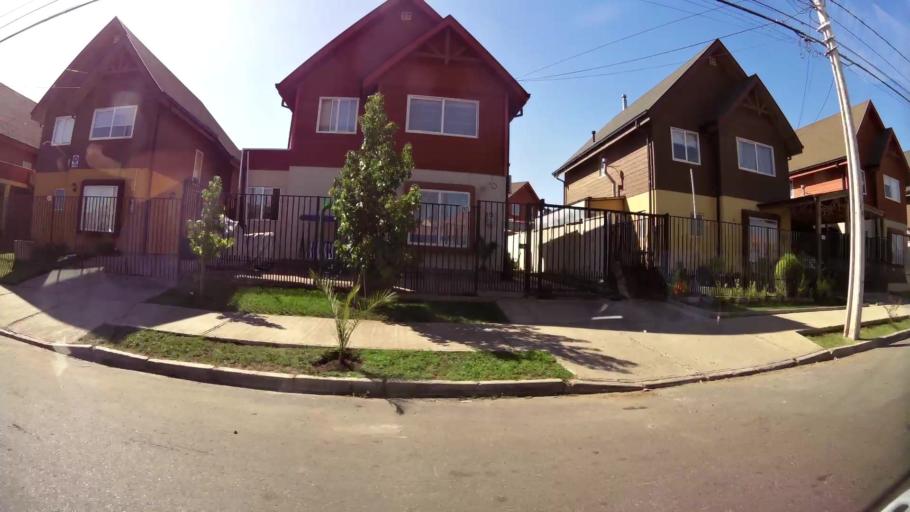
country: CL
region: Maule
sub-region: Provincia de Talca
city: Talca
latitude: -35.4208
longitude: -71.6134
